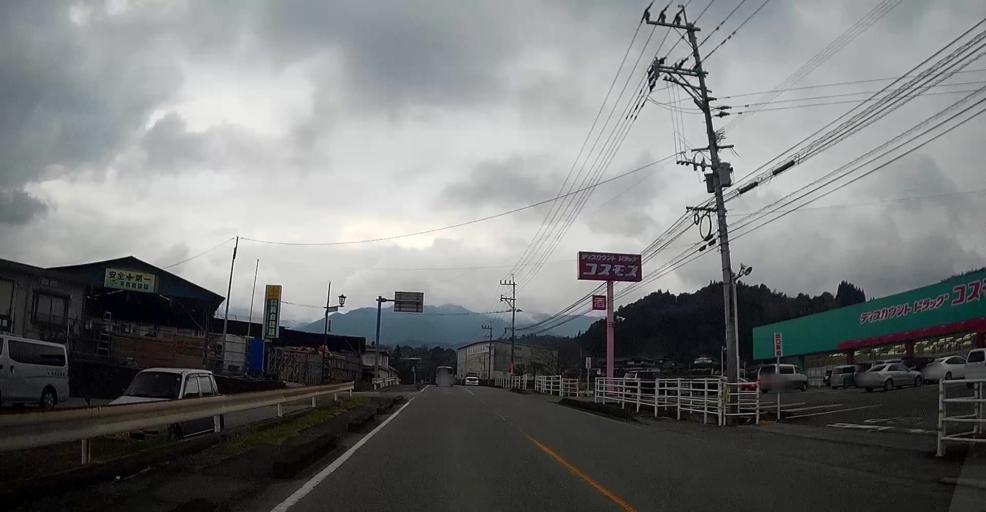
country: JP
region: Kumamoto
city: Matsubase
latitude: 32.6242
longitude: 130.8143
